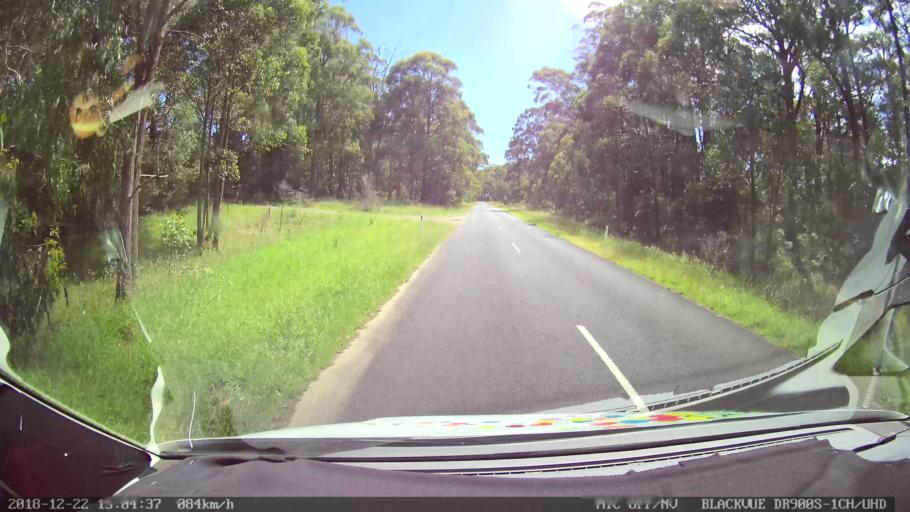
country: AU
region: New South Wales
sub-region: Bellingen
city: Dorrigo
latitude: -30.2764
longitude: 152.4368
